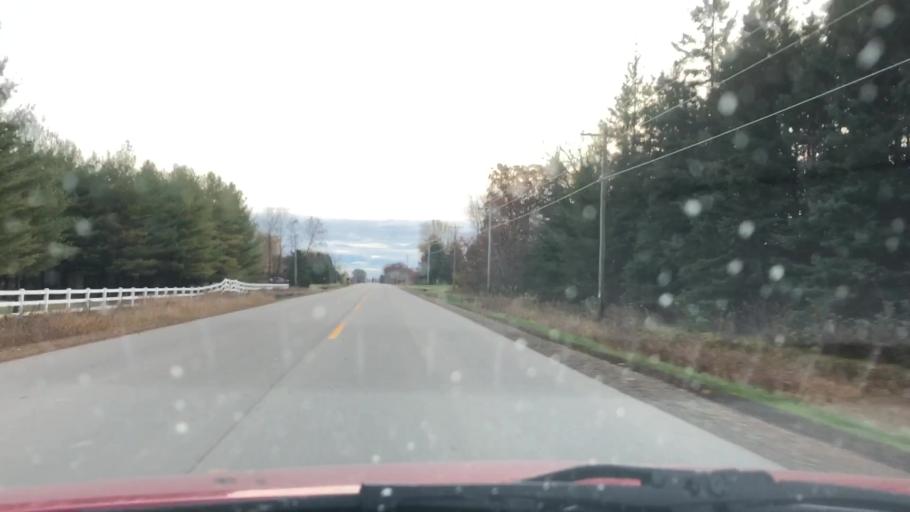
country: US
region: Wisconsin
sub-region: Outagamie County
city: Seymour
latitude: 44.4150
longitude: -88.2830
